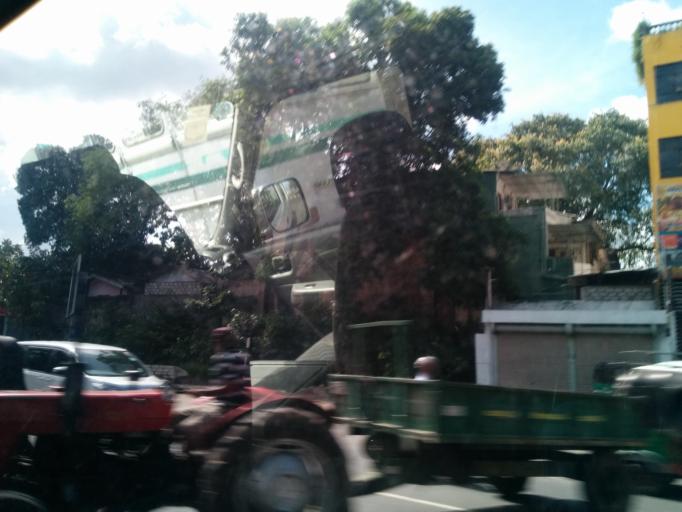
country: LK
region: Western
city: Kolonnawa
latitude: 6.9493
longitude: 79.8723
